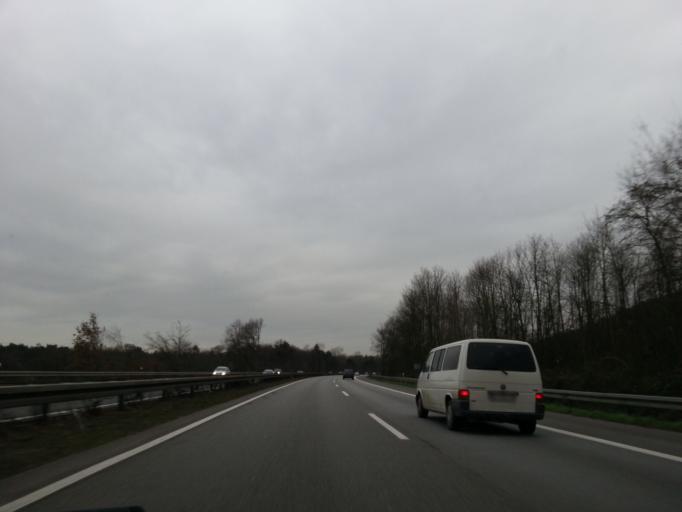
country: DE
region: North Rhine-Westphalia
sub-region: Regierungsbezirk Dusseldorf
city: Hunxe
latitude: 51.6071
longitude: 6.7792
